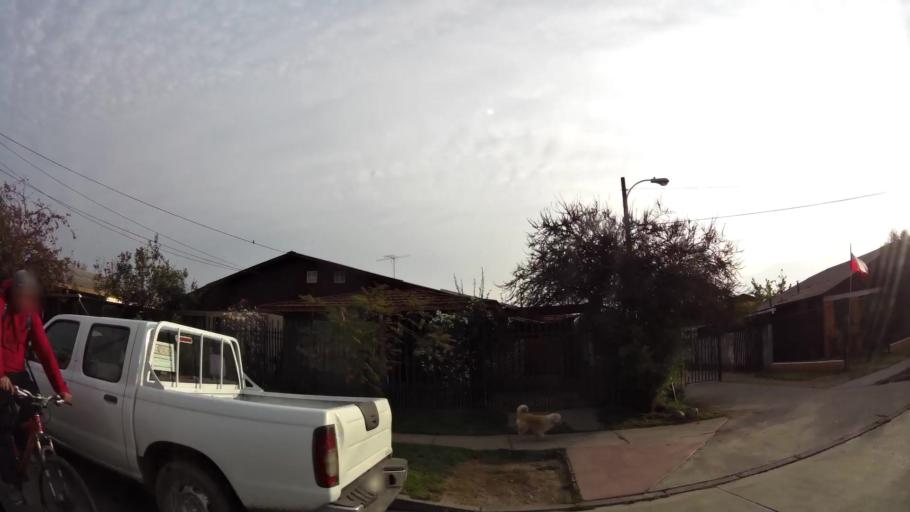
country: CL
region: Santiago Metropolitan
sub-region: Provincia de Maipo
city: San Bernardo
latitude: -33.5329
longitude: -70.7675
